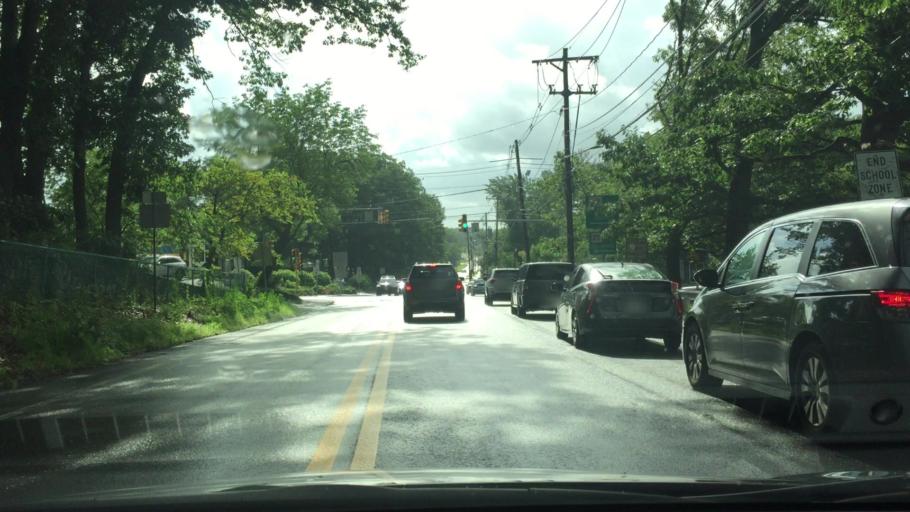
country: US
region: Massachusetts
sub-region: Middlesex County
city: Acton
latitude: 42.4749
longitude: -71.4546
